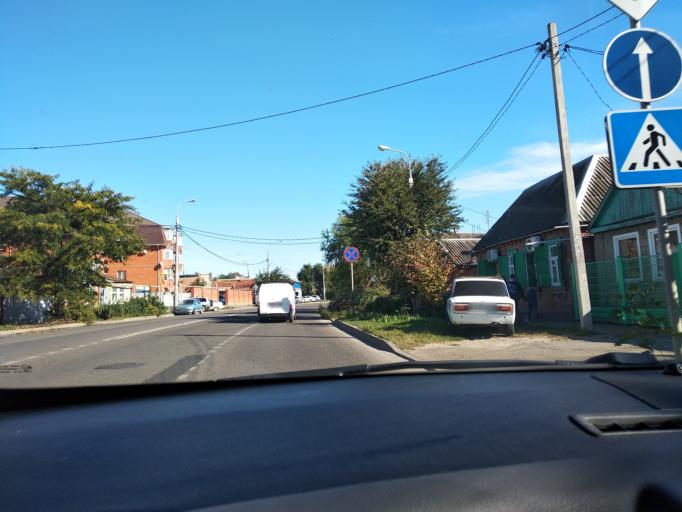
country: RU
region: Krasnodarskiy
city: Krasnodar
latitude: 45.0162
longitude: 38.9938
